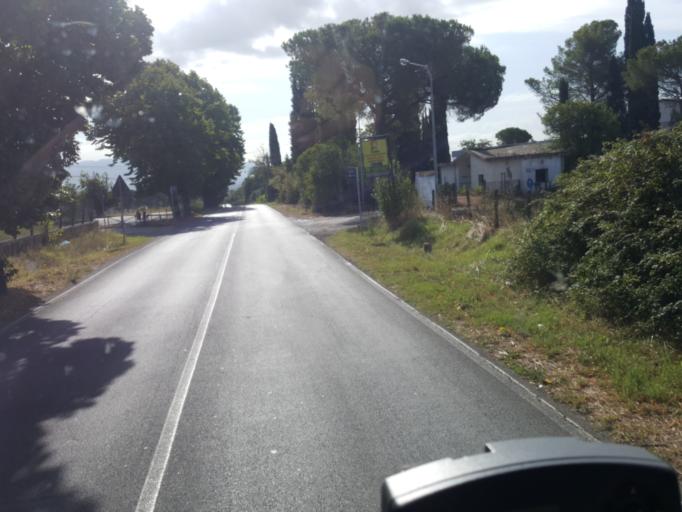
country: IT
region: Latium
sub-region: Citta metropolitana di Roma Capitale
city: Capena
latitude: 42.1304
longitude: 12.5646
